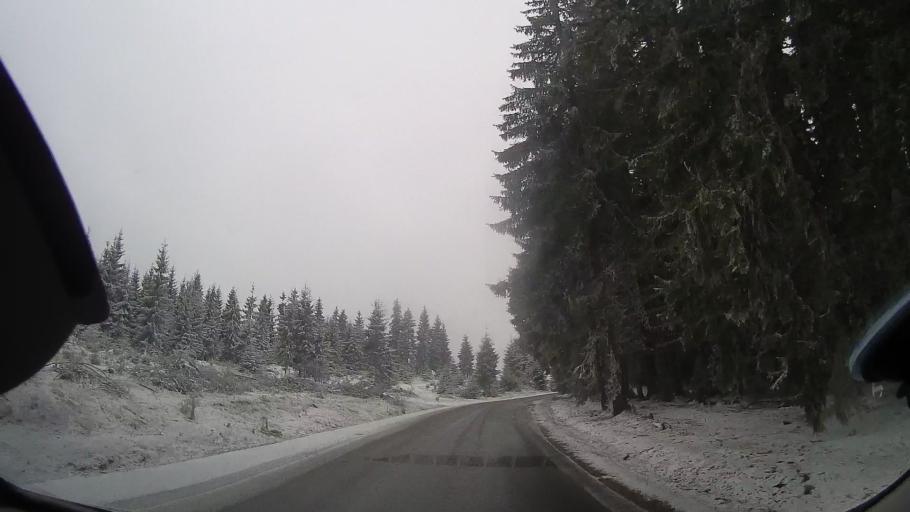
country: RO
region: Cluj
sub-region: Comuna Belis
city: Belis
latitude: 46.6387
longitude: 23.0548
